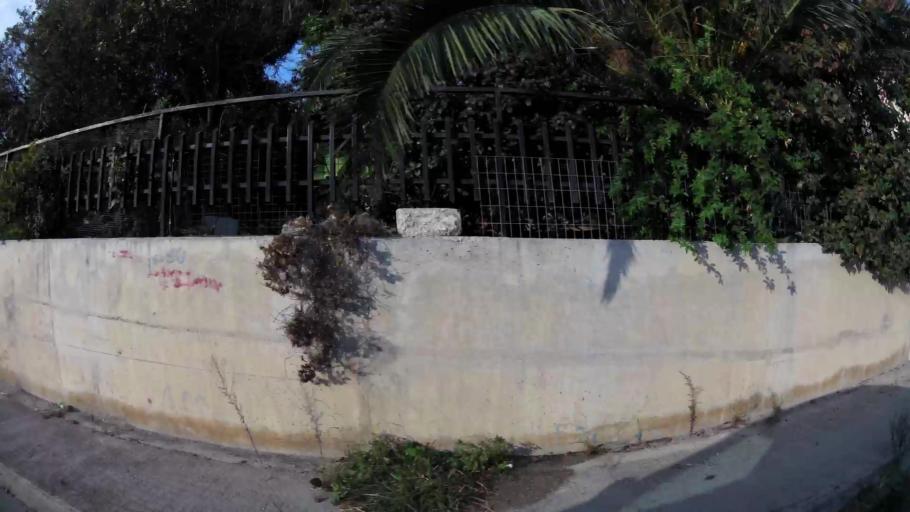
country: GR
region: Attica
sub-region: Nomarchia Dytikis Attikis
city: Zefyri
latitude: 38.0672
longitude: 23.7121
